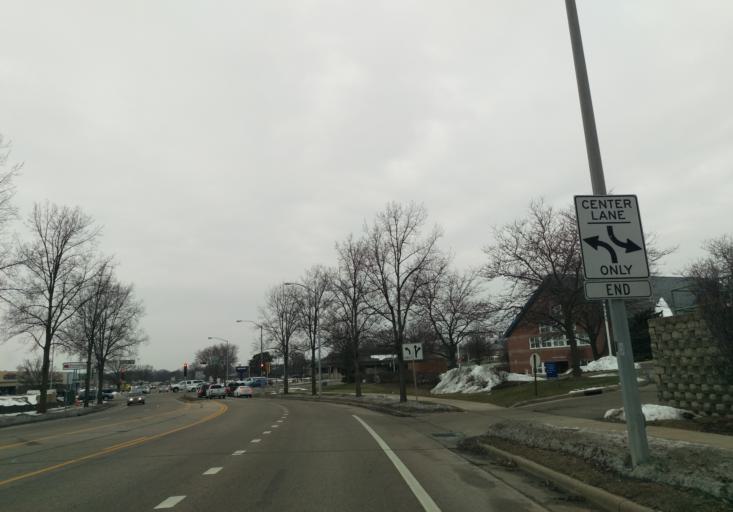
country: US
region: Wisconsin
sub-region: Dane County
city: Monona
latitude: 43.1297
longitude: -89.3036
